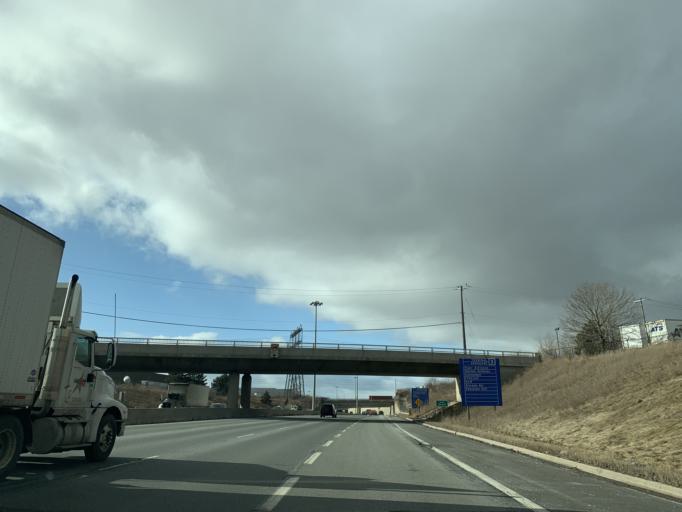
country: CA
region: Ontario
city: Etobicoke
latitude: 43.6986
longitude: -79.5793
